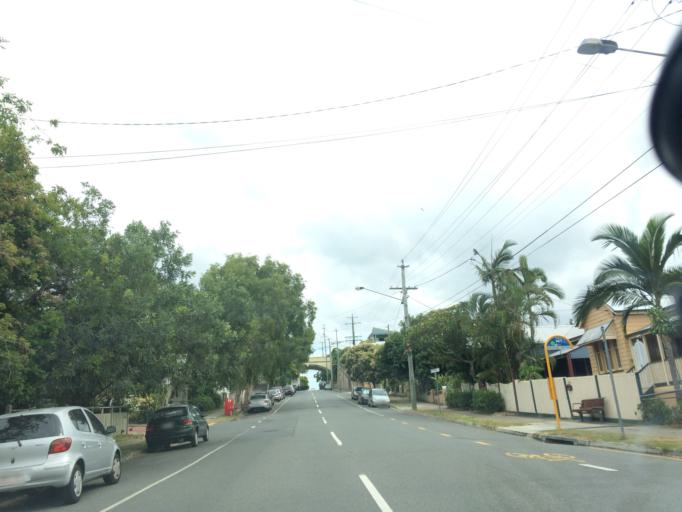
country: AU
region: Queensland
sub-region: Brisbane
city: South Brisbane
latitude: -27.4850
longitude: 153.0113
